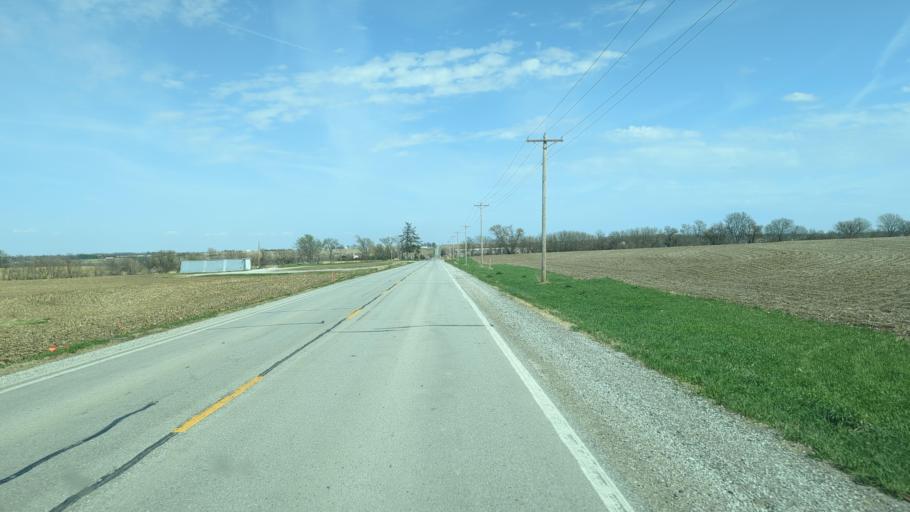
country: US
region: Nebraska
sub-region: Sarpy County
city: Springfield
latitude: 41.0889
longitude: -96.1523
